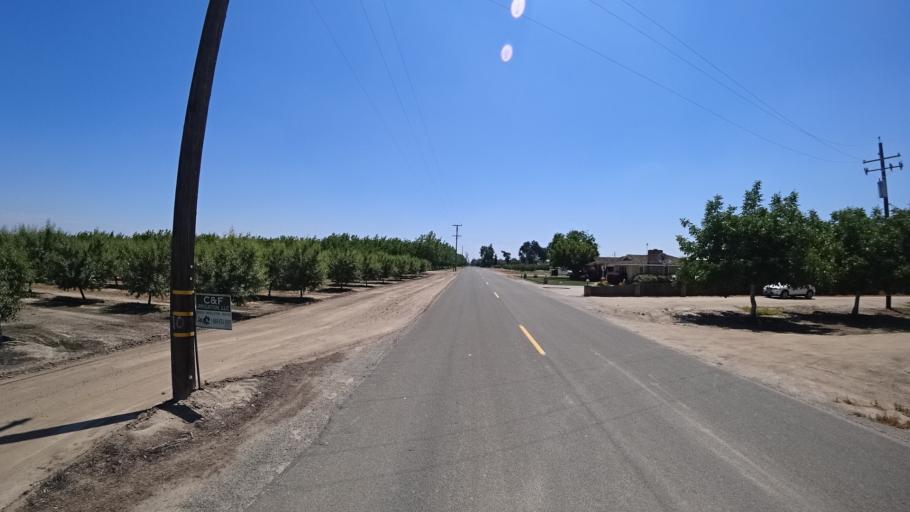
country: US
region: California
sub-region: Kings County
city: Lucerne
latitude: 36.4091
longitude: -119.6548
